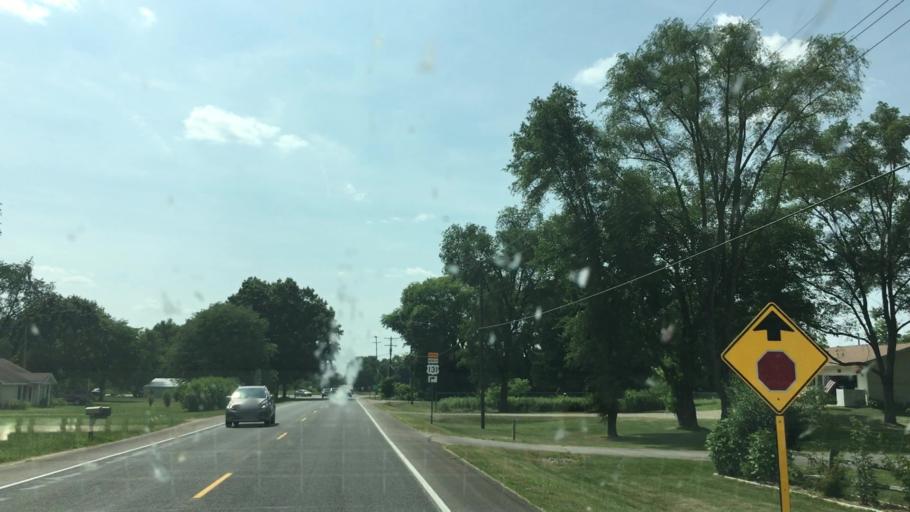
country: US
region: Michigan
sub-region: Allegan County
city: Plainwell
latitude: 42.4645
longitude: -85.6393
